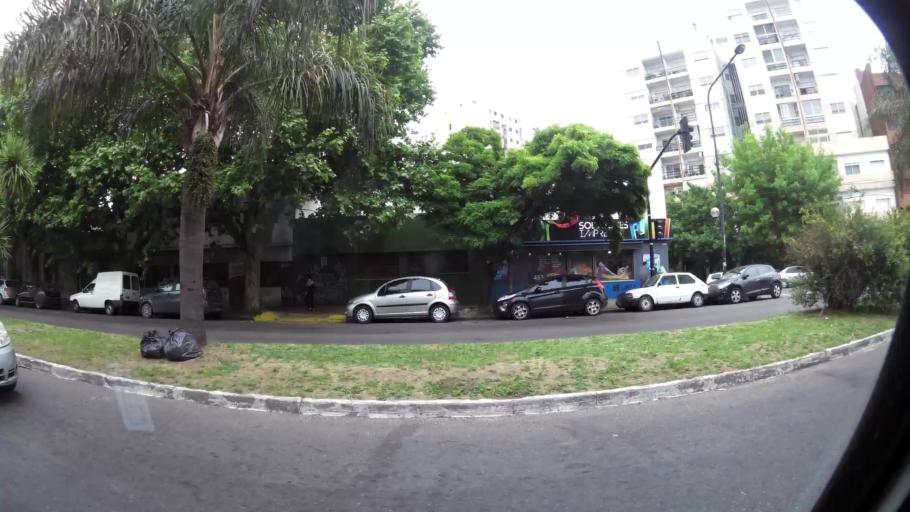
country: AR
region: Buenos Aires
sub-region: Partido de La Plata
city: La Plata
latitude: -34.9290
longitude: -57.9540
